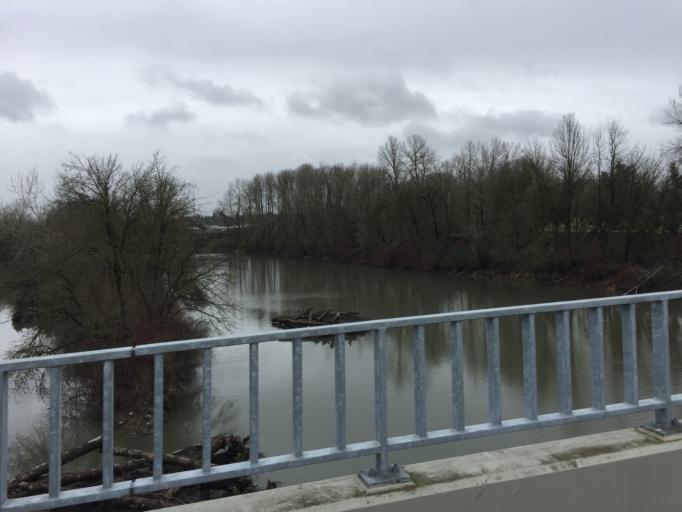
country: US
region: Washington
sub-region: Clark County
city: Vancouver
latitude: 45.5981
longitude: -122.7150
